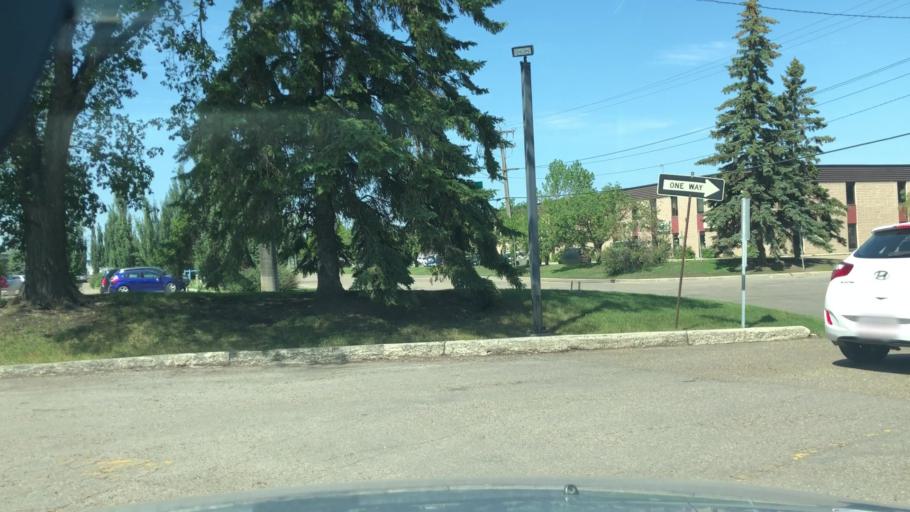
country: CA
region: Alberta
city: St. Albert
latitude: 53.5734
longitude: -113.5967
